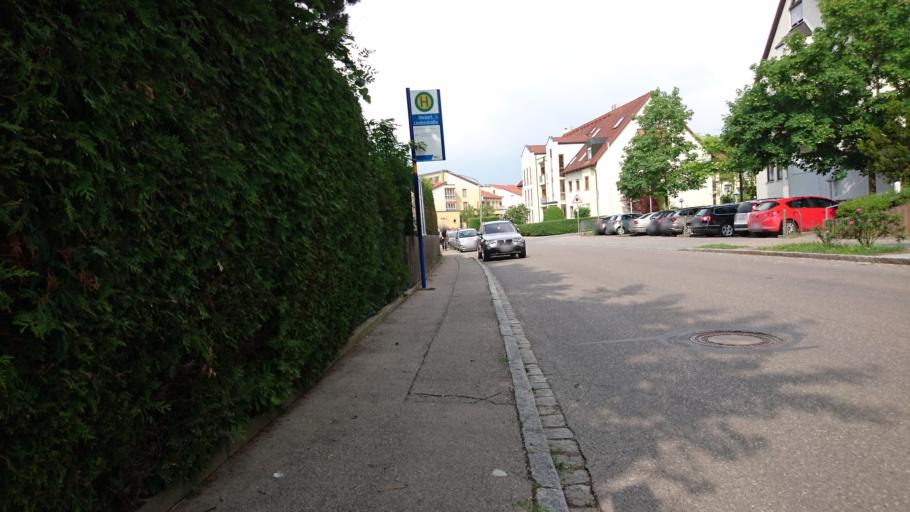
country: DE
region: Bavaria
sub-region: Swabia
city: Diedorf
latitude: 48.3559
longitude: 10.7863
